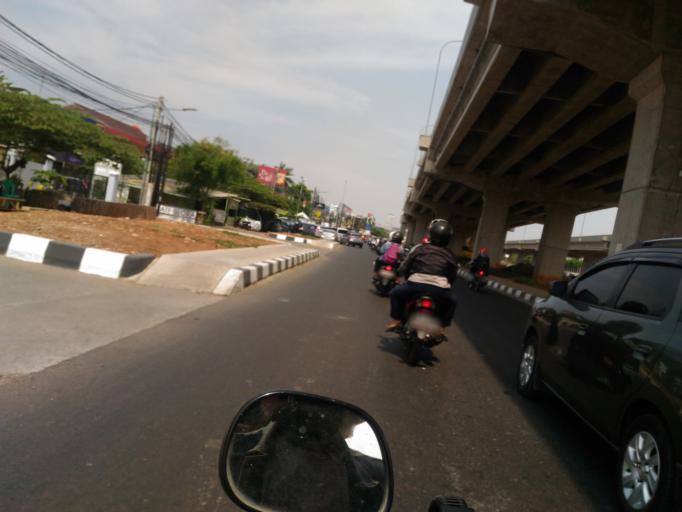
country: ID
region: West Java
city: Bekasi
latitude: -6.2481
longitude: 106.9279
